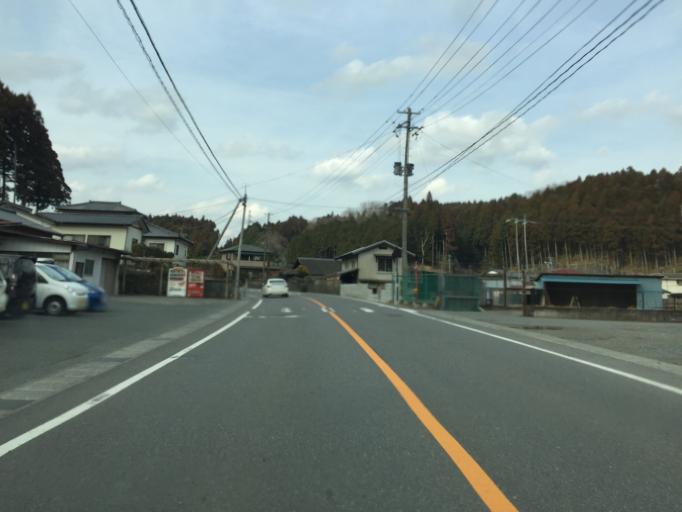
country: JP
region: Fukushima
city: Iwaki
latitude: 36.9771
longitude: 140.7391
